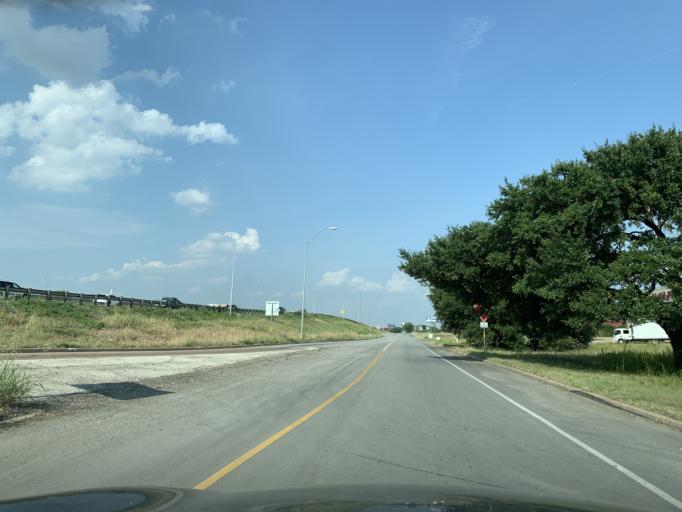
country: US
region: Texas
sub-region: Tarrant County
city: Haltom City
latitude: 32.7912
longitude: -97.2467
